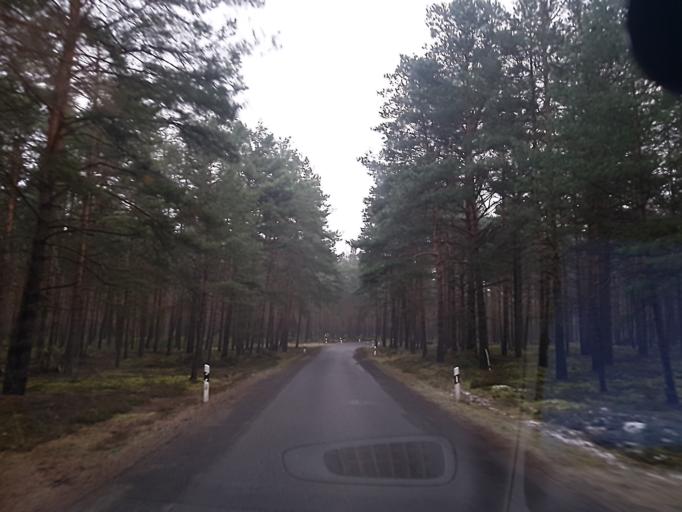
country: DE
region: Brandenburg
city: Crinitz
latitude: 51.7008
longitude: 13.7519
